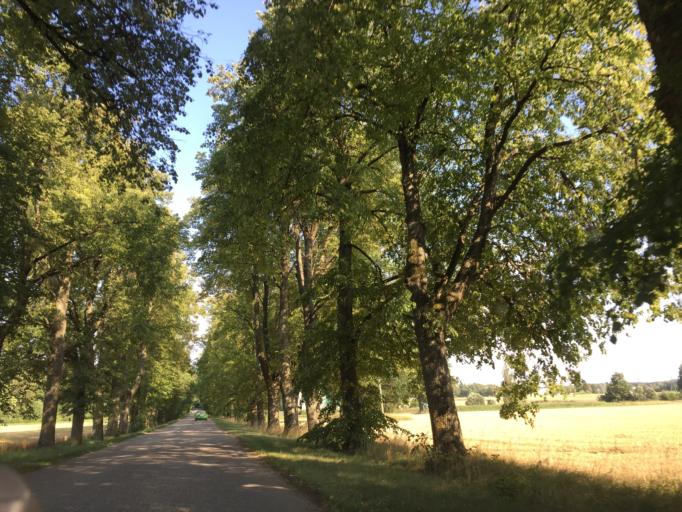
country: LT
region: Siauliu apskritis
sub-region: Joniskis
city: Joniskis
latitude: 56.4247
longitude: 23.6900
